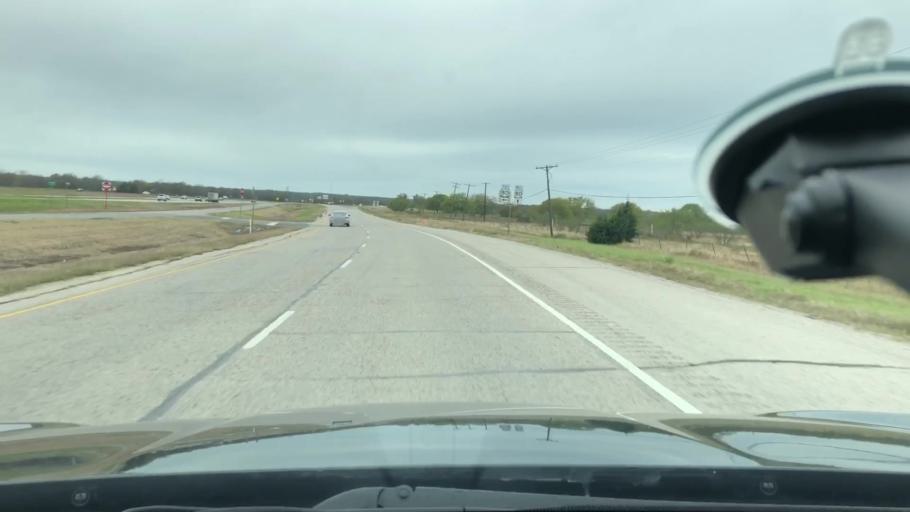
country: US
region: Texas
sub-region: Kaufman County
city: Talty
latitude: 32.7407
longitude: -96.3636
